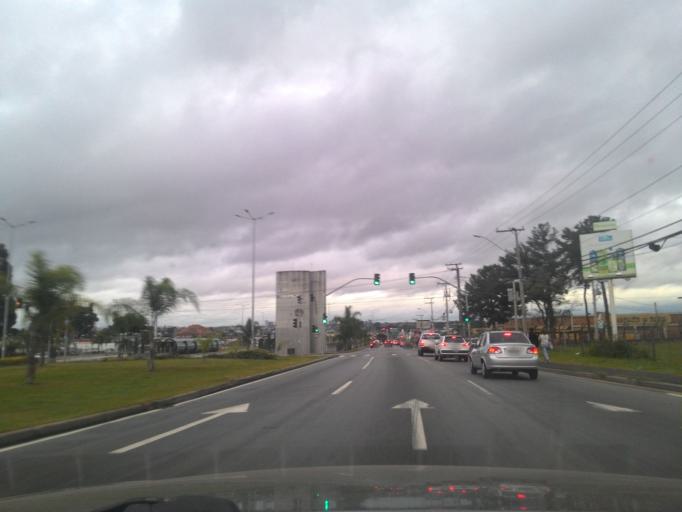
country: BR
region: Parana
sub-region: Curitiba
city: Curitiba
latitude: -25.4863
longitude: -49.2674
